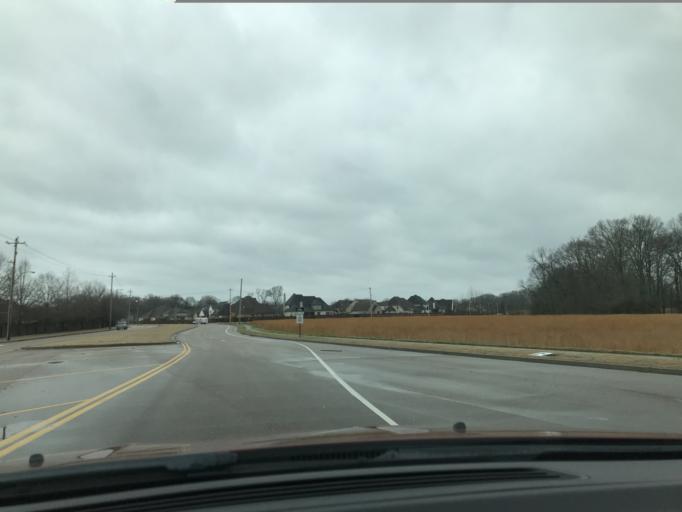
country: US
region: Tennessee
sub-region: Shelby County
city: Collierville
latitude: 35.0893
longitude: -89.7077
